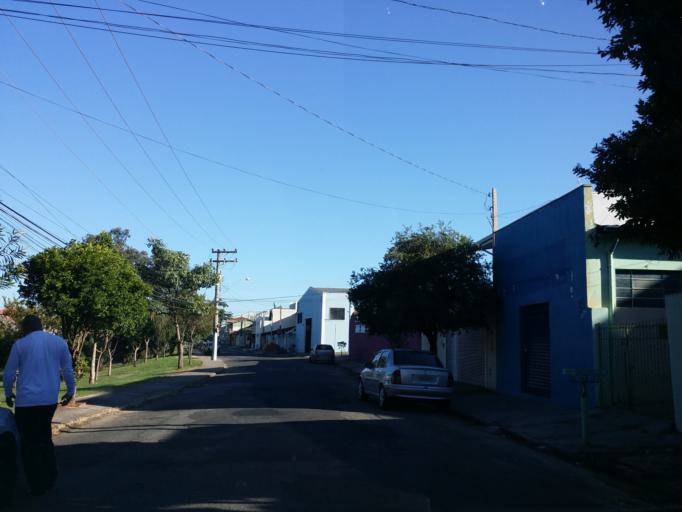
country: BR
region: Sao Paulo
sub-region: Indaiatuba
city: Indaiatuba
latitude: -23.0952
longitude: -47.1992
